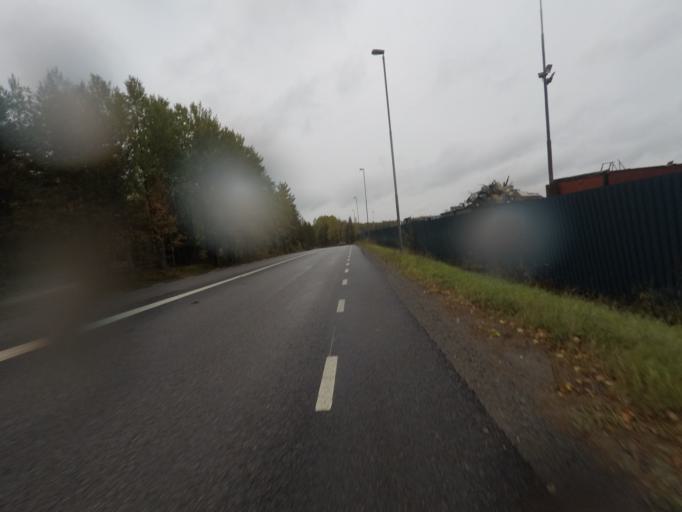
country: SE
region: OErebro
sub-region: Karlskoga Kommun
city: Karlskoga
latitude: 59.3195
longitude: 14.4738
